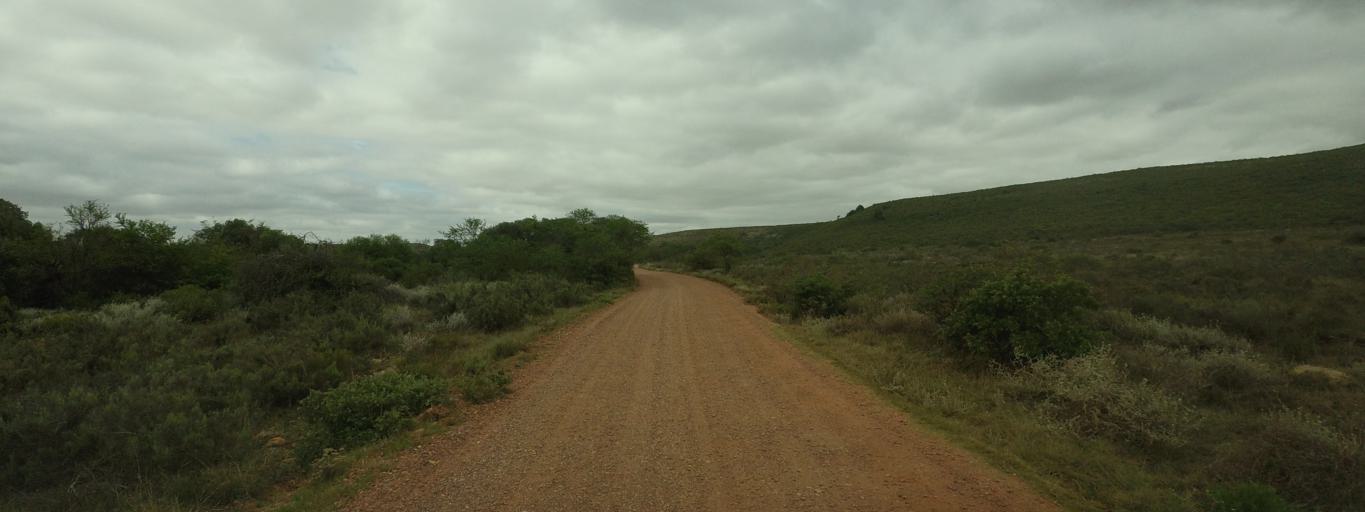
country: ZA
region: Western Cape
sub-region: Overberg District Municipality
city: Swellendam
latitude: -34.0653
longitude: 20.4380
